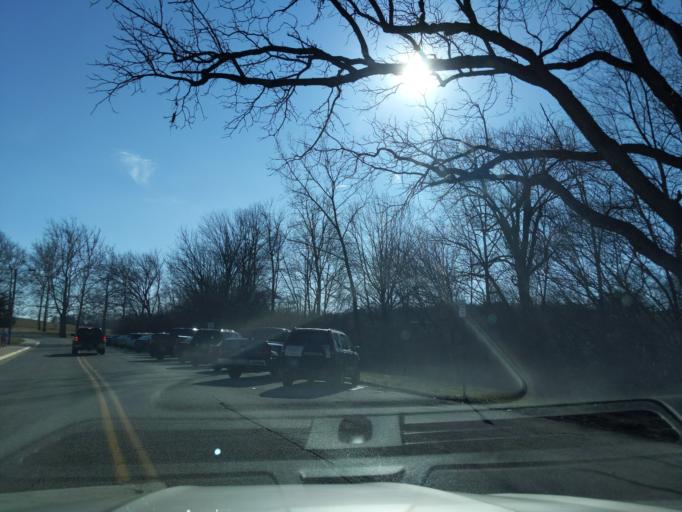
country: US
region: Indiana
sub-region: Tippecanoe County
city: West Lafayette
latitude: 40.4333
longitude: -86.9272
